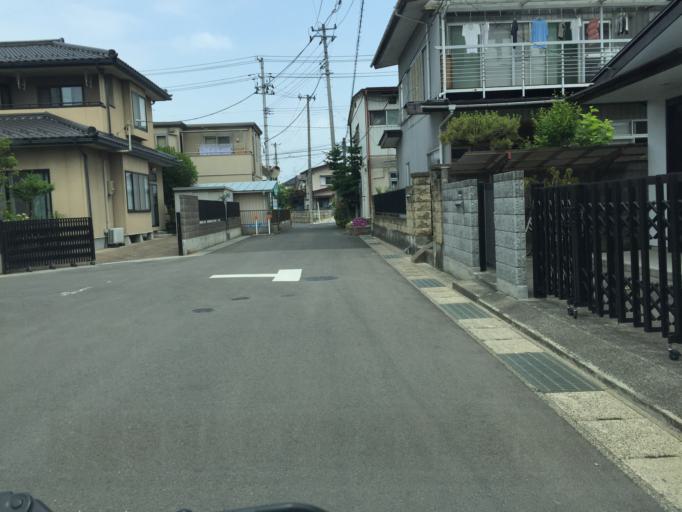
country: JP
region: Fukushima
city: Fukushima-shi
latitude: 37.7489
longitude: 140.4835
